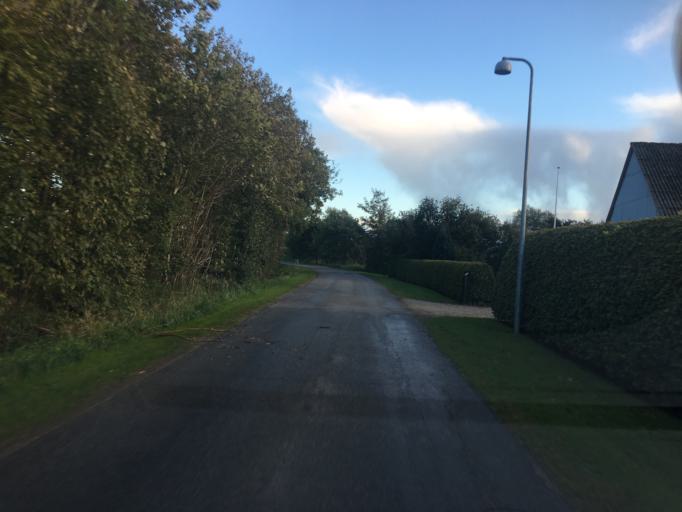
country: DE
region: Schleswig-Holstein
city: Ellhoft
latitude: 54.9614
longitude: 9.0125
